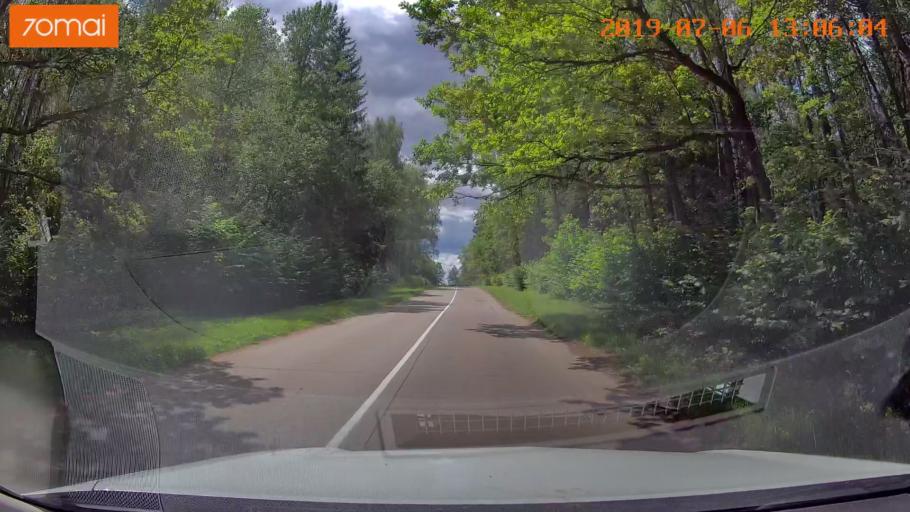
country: BY
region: Minsk
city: Dzyarzhynsk
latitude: 53.6844
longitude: 27.0583
